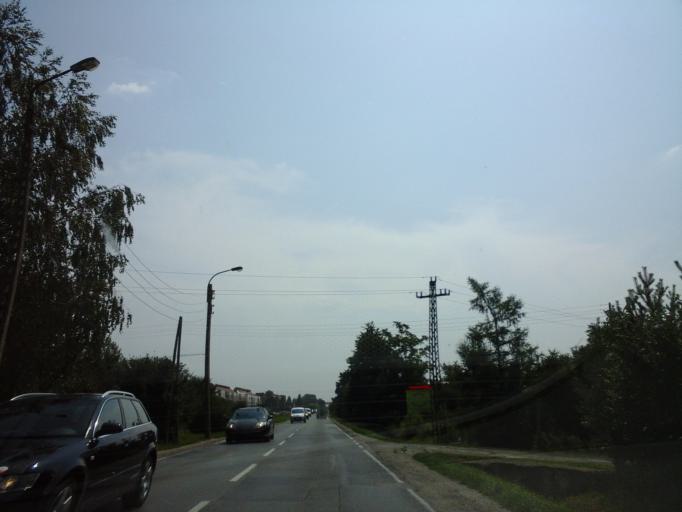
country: PL
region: Lower Silesian Voivodeship
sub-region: Powiat wroclawski
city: Zerniki Wroclawskie
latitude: 51.0575
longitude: 17.0570
